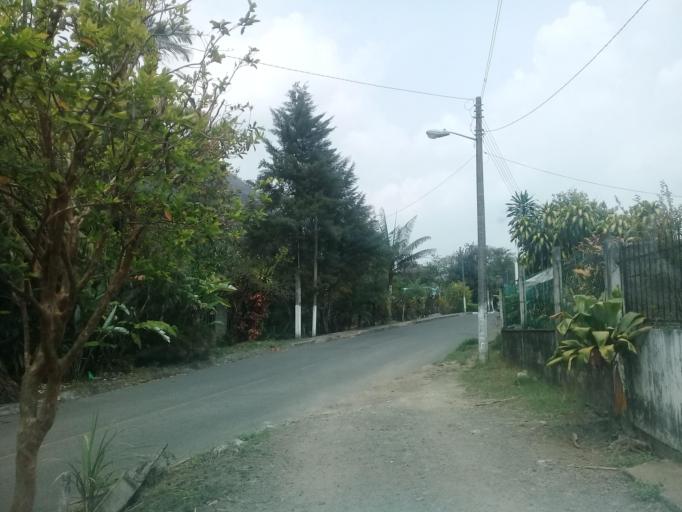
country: MX
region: Veracruz
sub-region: Cordoba
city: Fredepo
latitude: 18.8568
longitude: -96.9913
